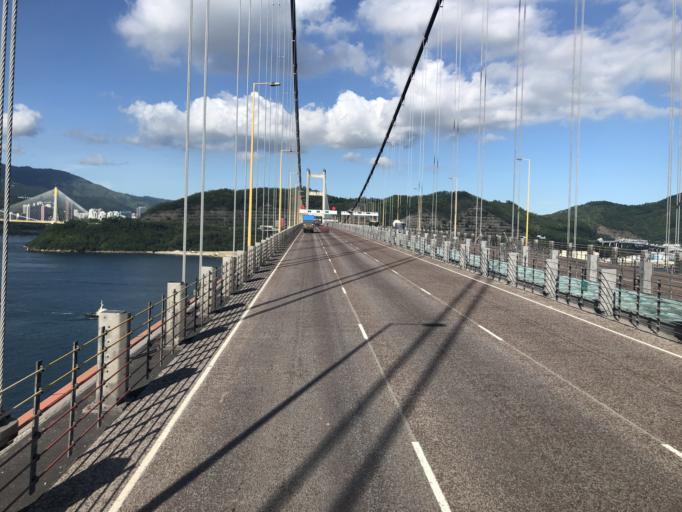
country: HK
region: Tsuen Wan
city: Tsuen Wan
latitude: 22.3497
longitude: 114.0685
